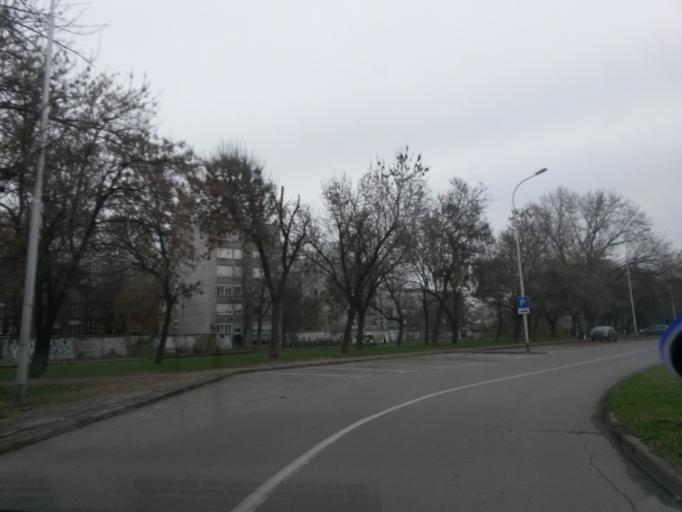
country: HR
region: Osjecko-Baranjska
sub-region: Grad Osijek
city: Osijek
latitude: 45.5532
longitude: 18.6965
